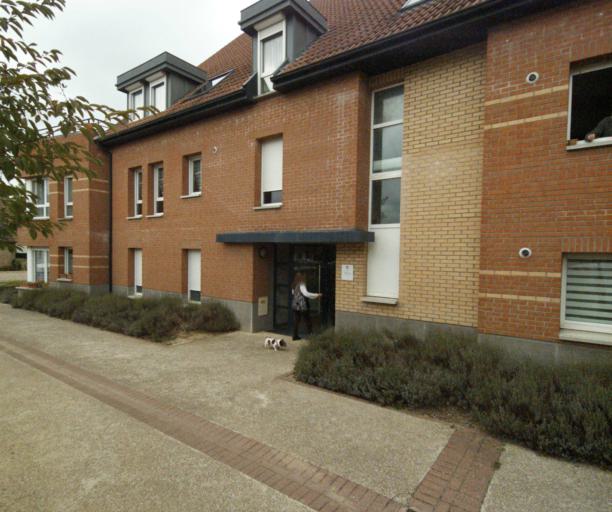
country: FR
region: Nord-Pas-de-Calais
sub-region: Departement du Nord
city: Marquillies
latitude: 50.5578
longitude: 2.8723
